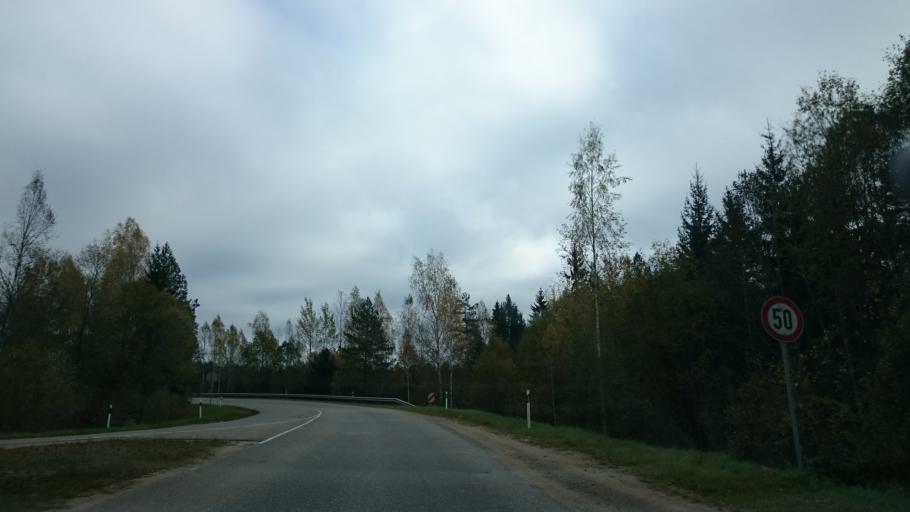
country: LV
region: Amatas Novads
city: Drabesi
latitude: 57.2259
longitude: 25.2530
